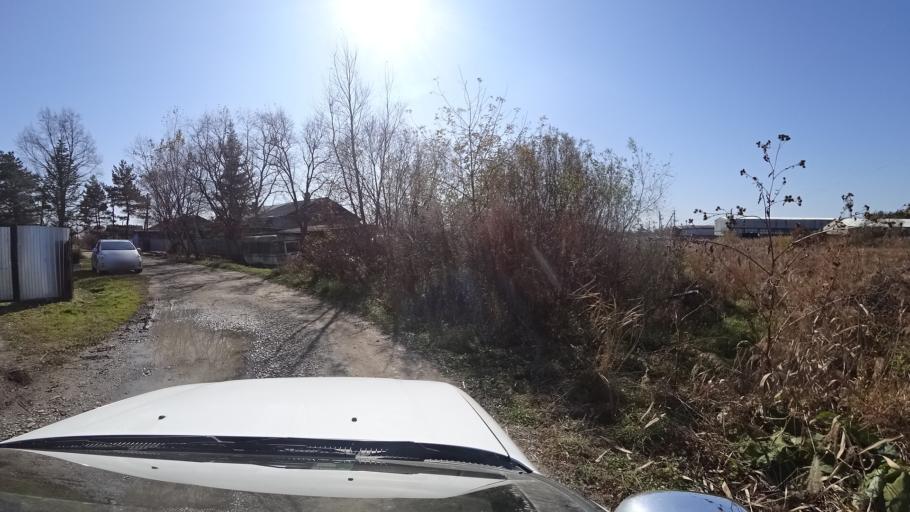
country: RU
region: Primorskiy
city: Dal'nerechensk
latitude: 45.9235
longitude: 133.7822
